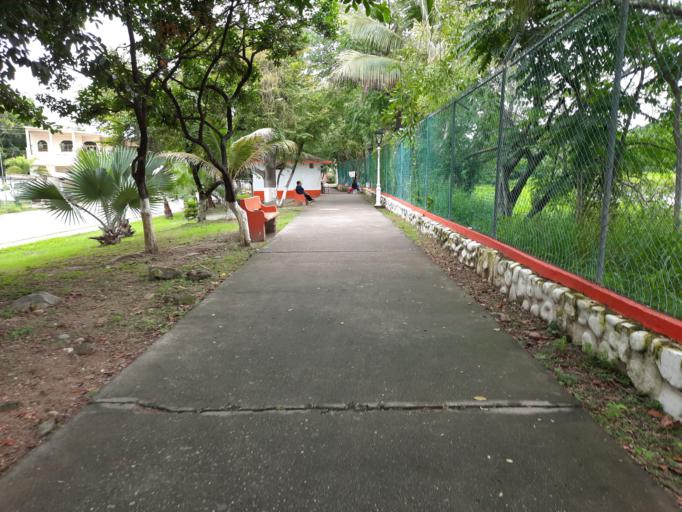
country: MX
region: Jalisco
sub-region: Puerto Vallarta
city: Puerto Vallarta
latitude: 20.6586
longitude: -105.2084
